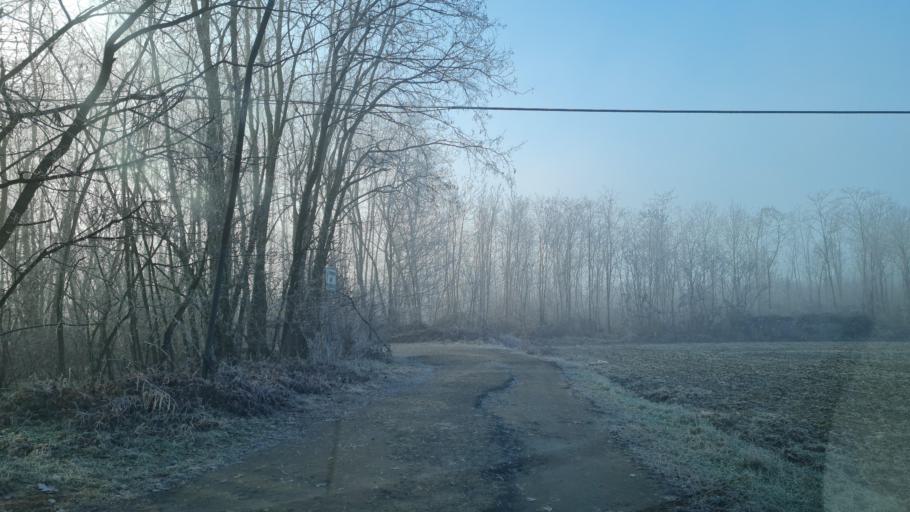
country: IT
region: Piedmont
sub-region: Provincia di Biella
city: Salussola
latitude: 45.4482
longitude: 8.1275
